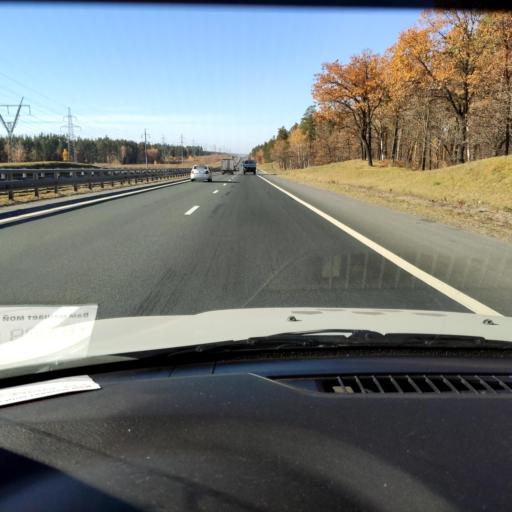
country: RU
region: Samara
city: Povolzhskiy
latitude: 53.5176
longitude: 49.7754
